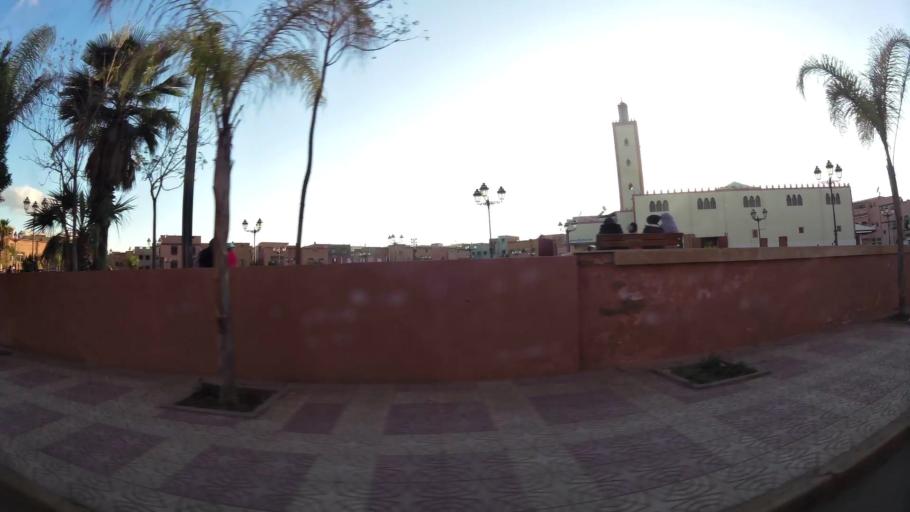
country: MA
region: Marrakech-Tensift-Al Haouz
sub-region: Kelaa-Des-Sraghna
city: Sidi Abdallah
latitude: 32.2372
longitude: -7.9522
